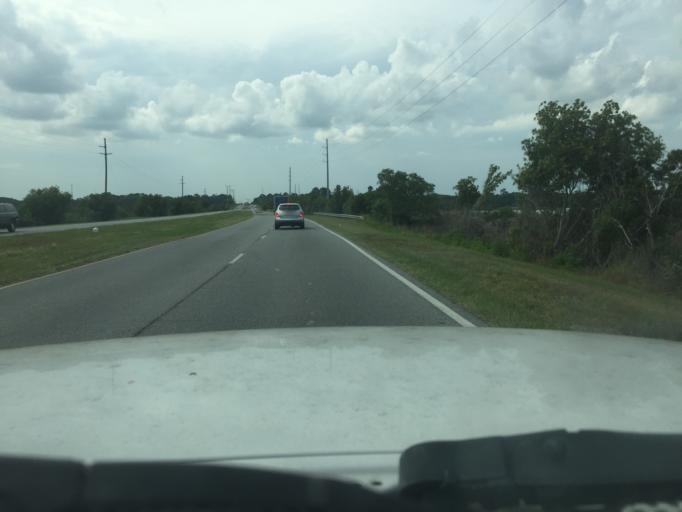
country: US
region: Georgia
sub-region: Chatham County
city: Whitemarsh Island
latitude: 32.0573
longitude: -81.0198
